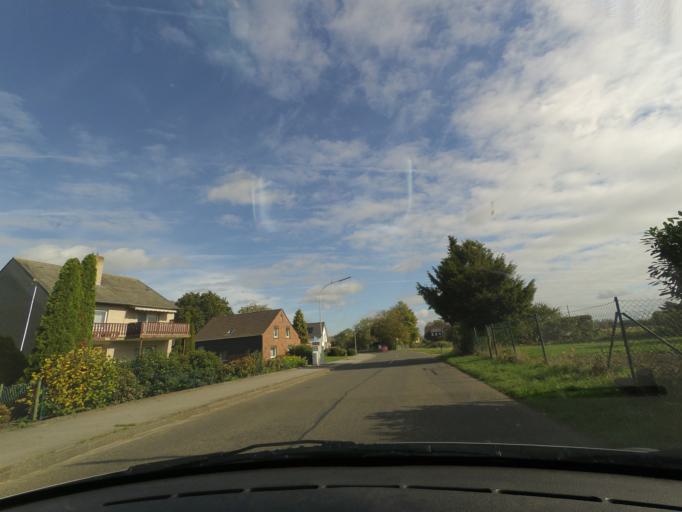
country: DE
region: North Rhine-Westphalia
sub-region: Regierungsbezirk Dusseldorf
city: Korschenbroich
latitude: 51.1714
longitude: 6.5436
